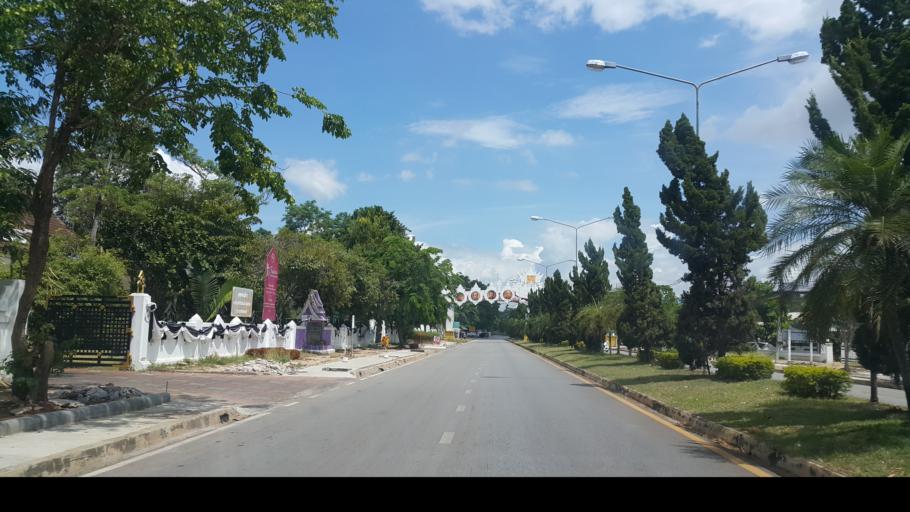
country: TH
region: Phayao
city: Phayao
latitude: 19.1749
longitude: 99.8922
